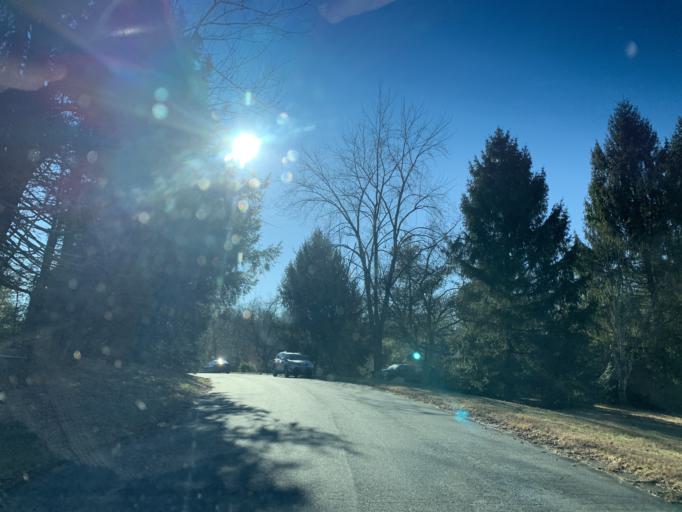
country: US
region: Maryland
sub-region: Harford County
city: Riverside
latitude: 39.5340
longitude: -76.2557
